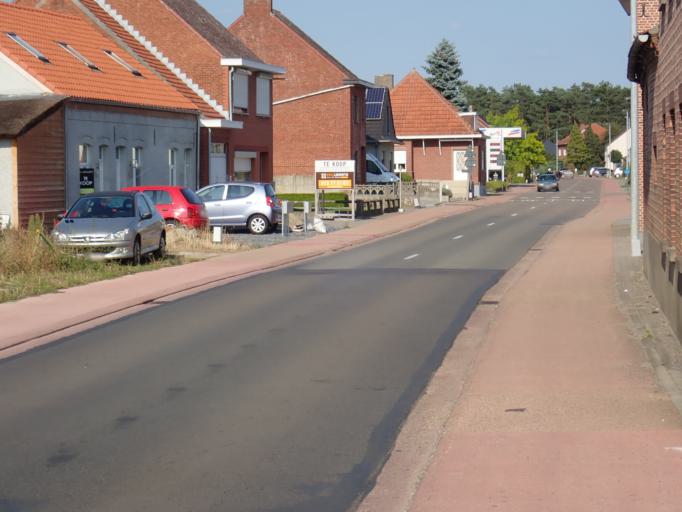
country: BE
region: Flanders
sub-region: Provincie Vlaams-Brabant
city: Scherpenheuvel-Zichem
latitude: 51.0209
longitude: 4.9641
